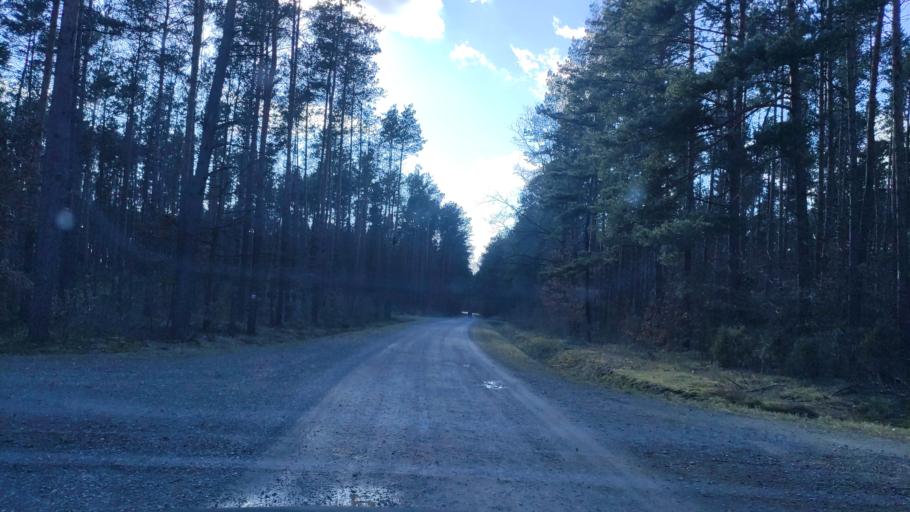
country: PL
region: Masovian Voivodeship
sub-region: Powiat radomski
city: Jastrzebia
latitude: 51.4697
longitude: 21.2405
